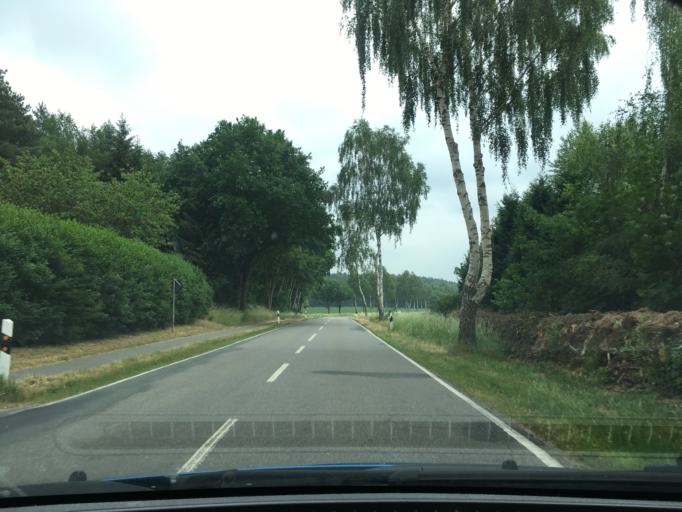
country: DE
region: Lower Saxony
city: Karwitz
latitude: 53.0657
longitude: 10.9557
